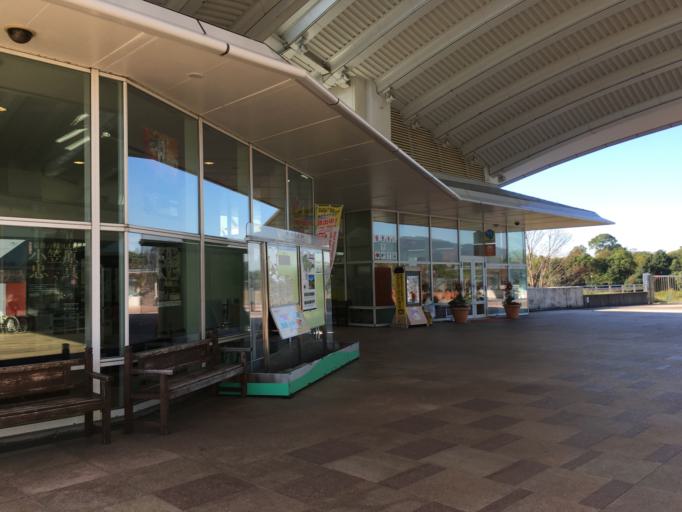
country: JP
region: Saga Prefecture
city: Kanzakimachi-kanzaki
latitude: 33.3240
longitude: 130.3888
